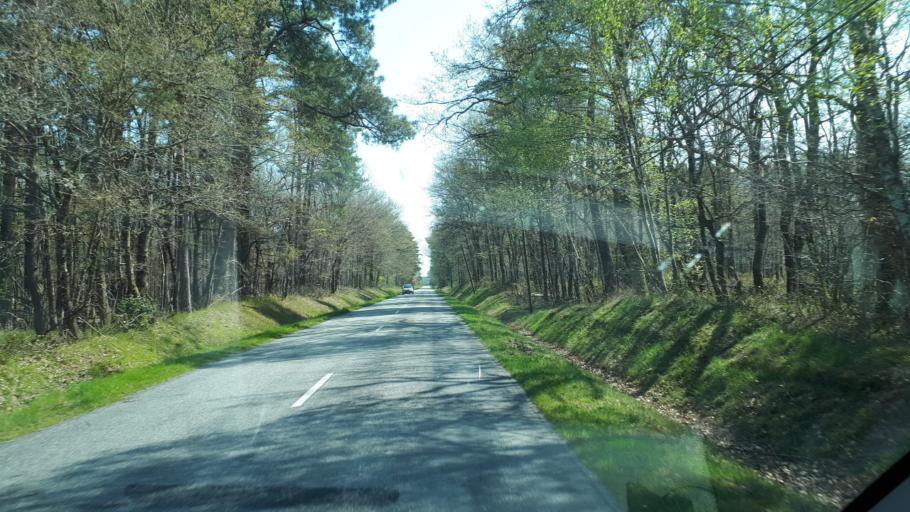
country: FR
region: Centre
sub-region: Departement du Loir-et-Cher
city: Theillay
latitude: 47.3137
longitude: 2.0717
